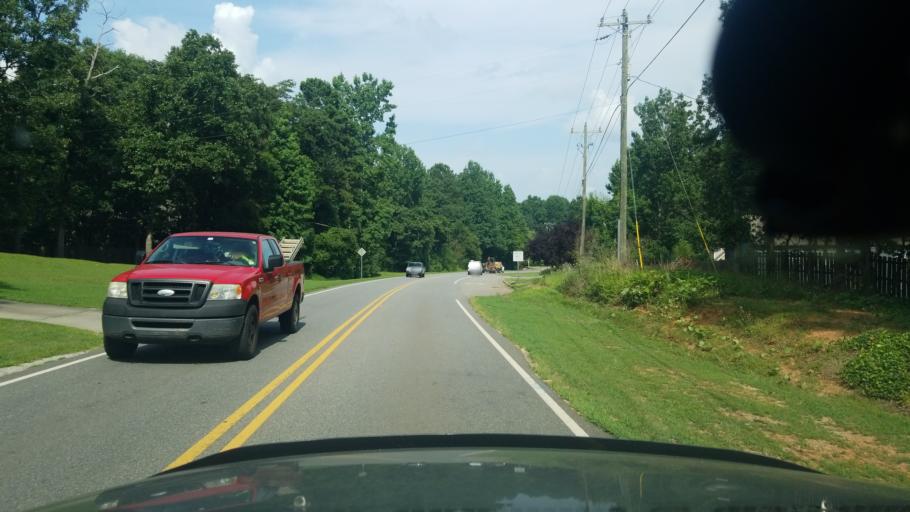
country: US
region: Georgia
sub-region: Dawson County
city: Dawsonville
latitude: 34.3133
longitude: -84.0769
